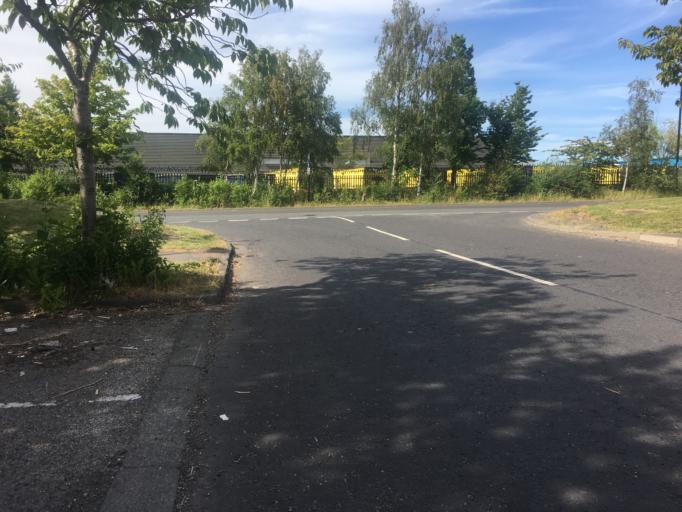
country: GB
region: England
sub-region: Sunderland
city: Washington
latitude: 54.8847
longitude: -1.5375
